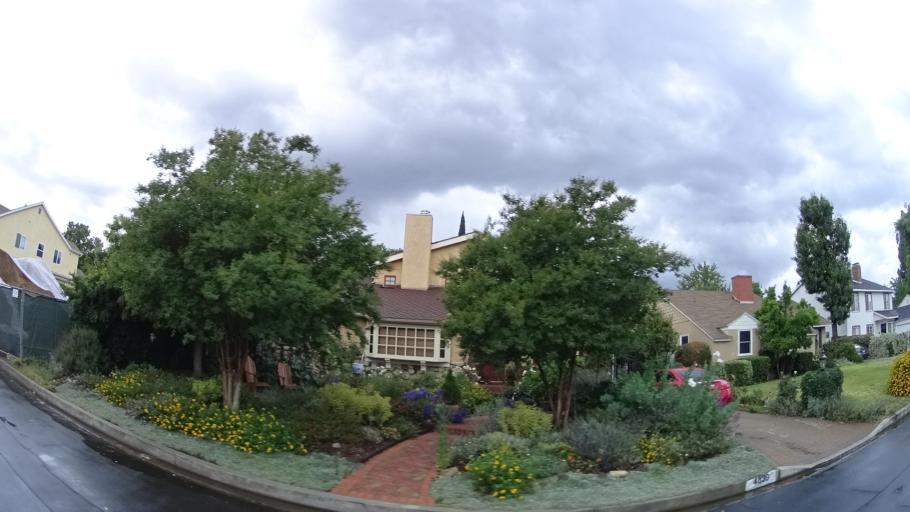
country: US
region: California
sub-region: Los Angeles County
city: Sherman Oaks
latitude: 34.1588
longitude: -118.4335
